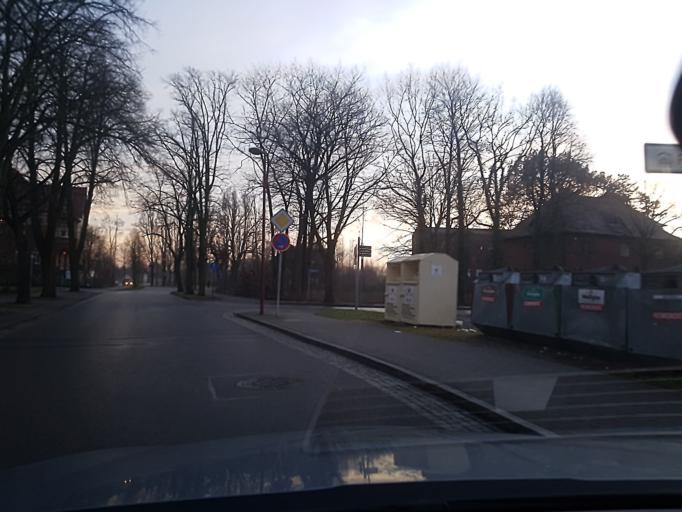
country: DE
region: Brandenburg
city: Finsterwalde
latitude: 51.6297
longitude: 13.7014
